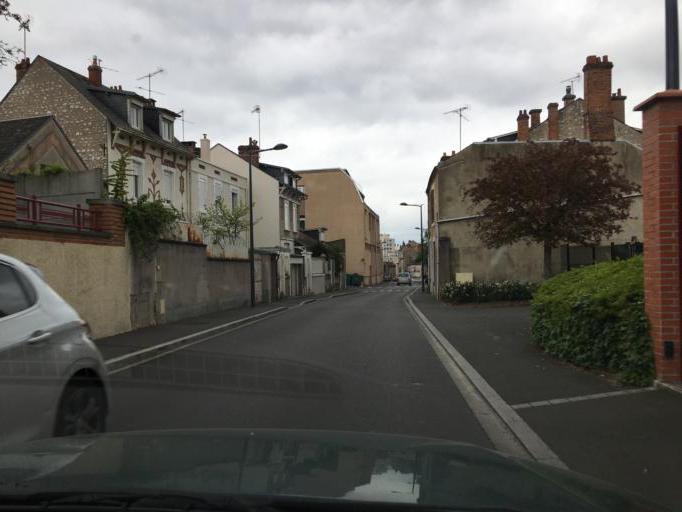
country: FR
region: Centre
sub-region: Departement du Loiret
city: Orleans
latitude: 47.9058
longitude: 1.8874
